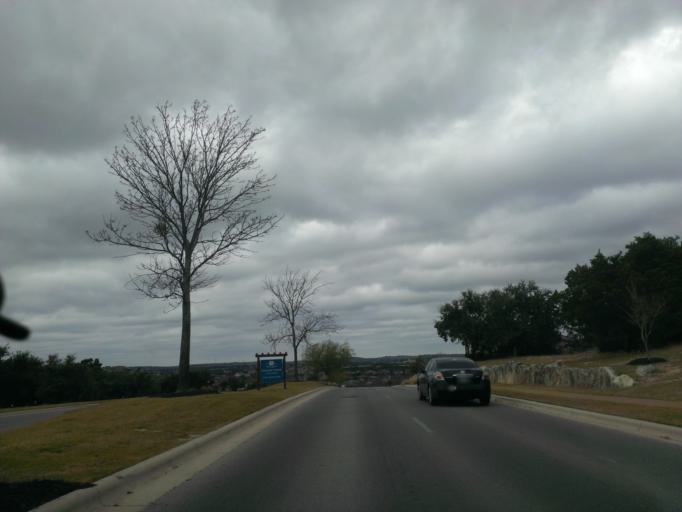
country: US
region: Texas
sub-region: Travis County
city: The Hills
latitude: 30.3509
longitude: -97.9991
